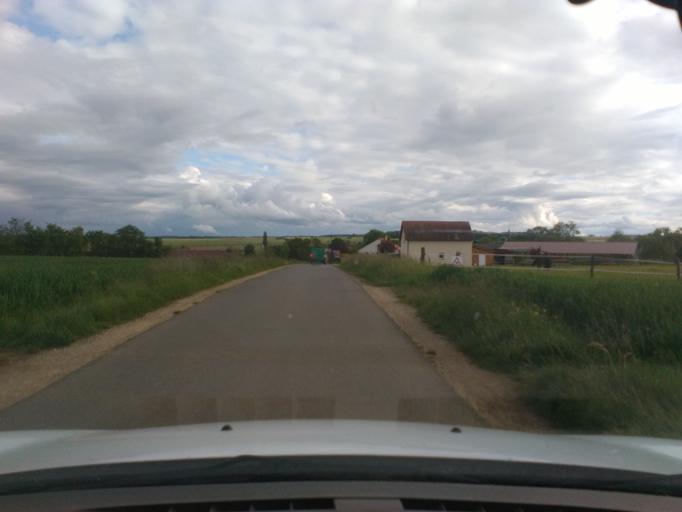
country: FR
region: Lorraine
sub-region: Departement des Vosges
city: Mirecourt
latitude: 48.3393
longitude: 6.1008
